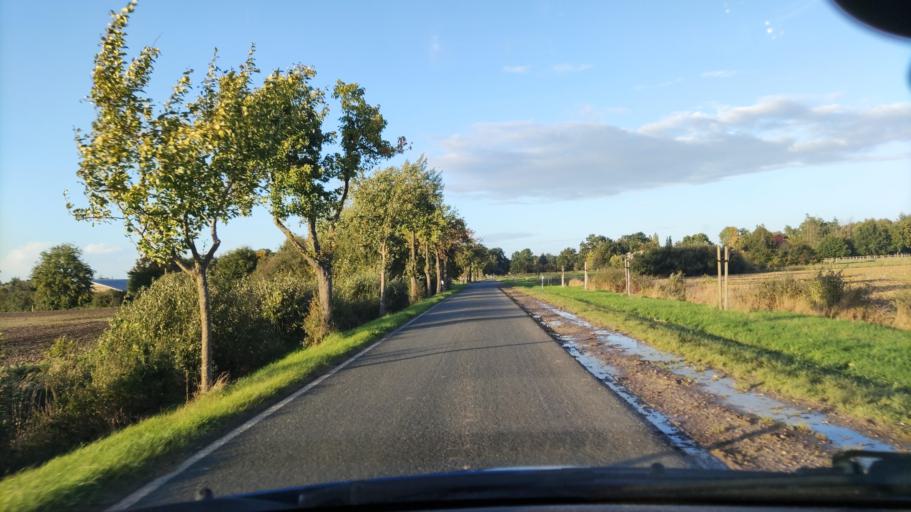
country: DE
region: Lower Saxony
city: Neu Darchau
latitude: 53.2835
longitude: 10.8742
